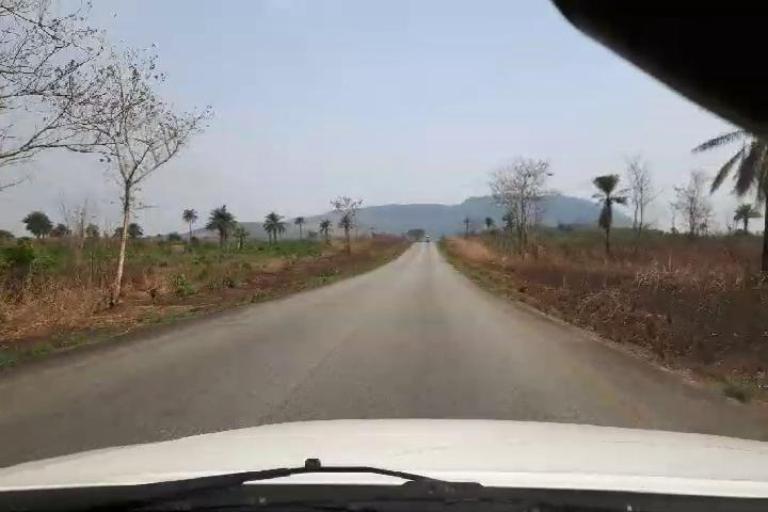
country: SL
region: Northern Province
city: Yonibana
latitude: 8.3924
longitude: -12.1929
